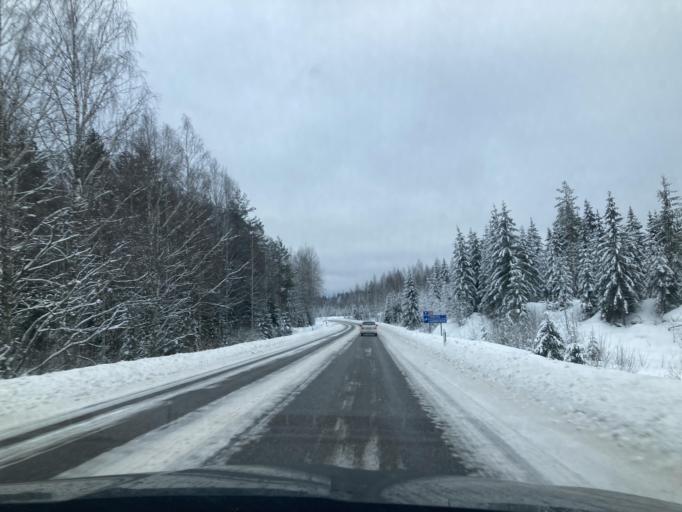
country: FI
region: Central Finland
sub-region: Jaemsae
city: Kuhmoinen
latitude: 61.5051
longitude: 25.1393
